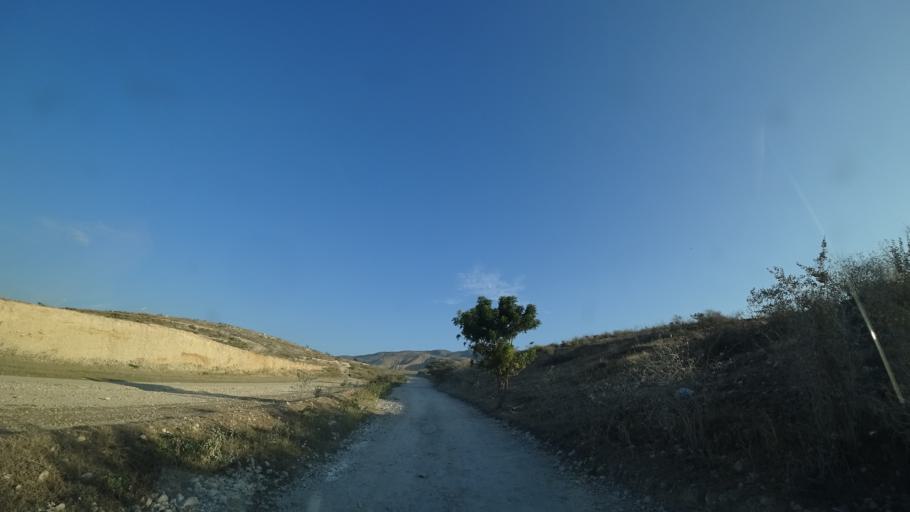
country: HT
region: Ouest
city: Cabaret
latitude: 18.6805
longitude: -72.3191
